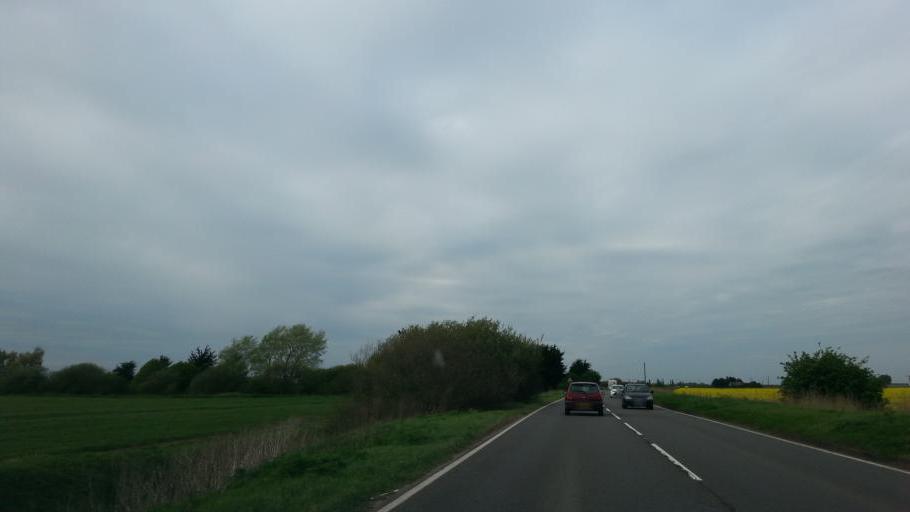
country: GB
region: England
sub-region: Cambridgeshire
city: March
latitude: 52.5820
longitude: 0.0569
